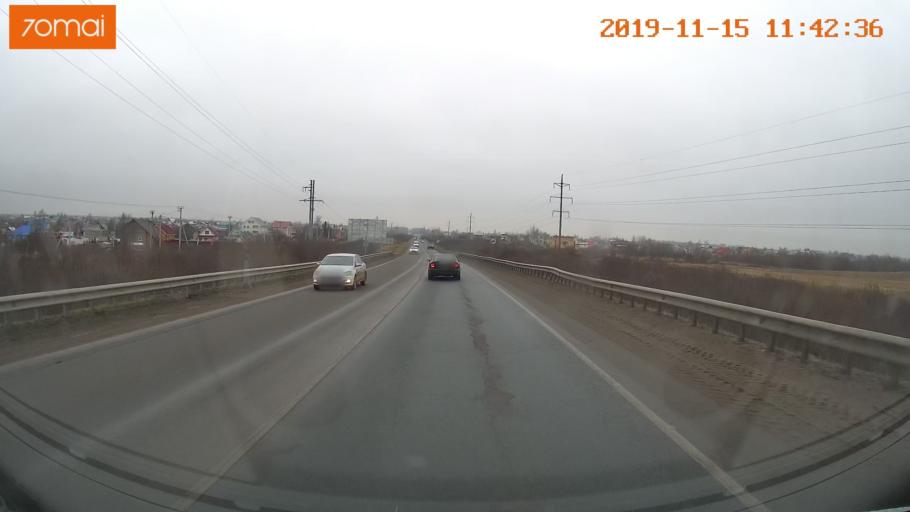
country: RU
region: Vologda
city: Vologda
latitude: 59.2201
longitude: 39.7746
